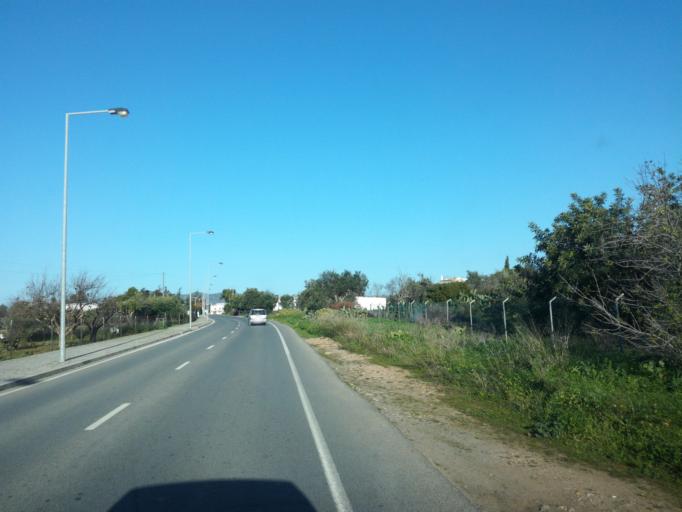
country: PT
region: Faro
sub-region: Olhao
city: Laranjeiro
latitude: 37.0547
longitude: -7.7586
